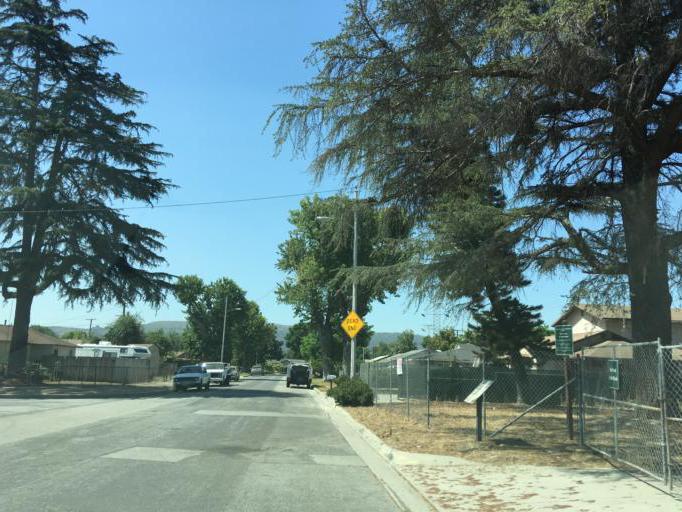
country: US
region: California
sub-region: Los Angeles County
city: Avocado Heights
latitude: 34.0502
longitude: -118.0048
